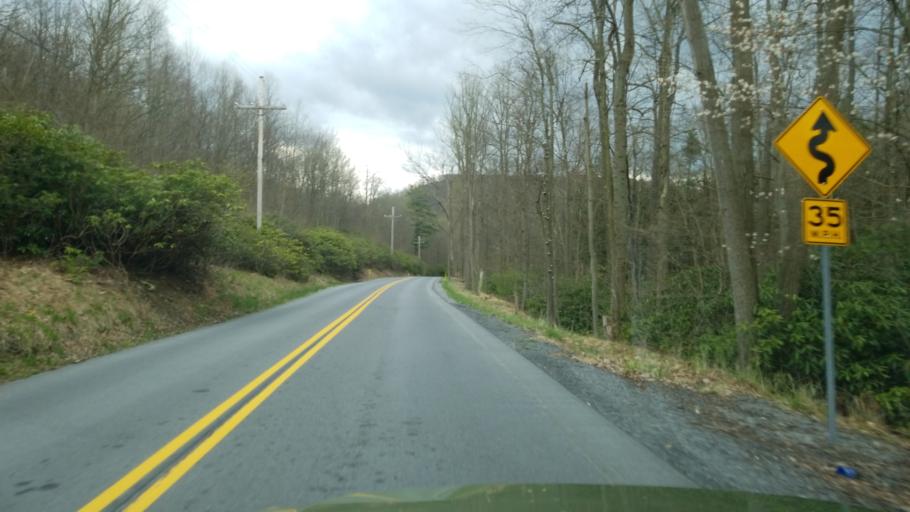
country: US
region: Pennsylvania
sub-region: Blair County
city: Tipton
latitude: 40.6634
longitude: -78.3325
